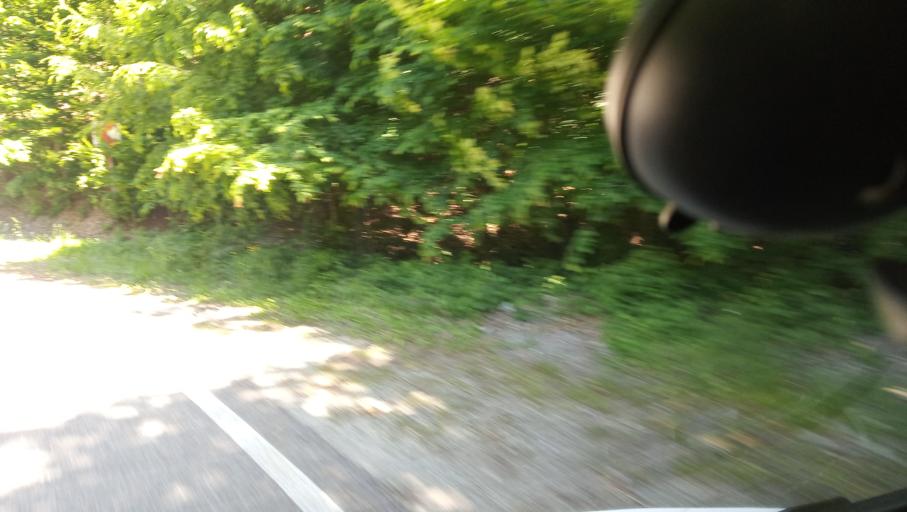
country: RO
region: Mehedinti
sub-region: Comuna Obarsia-Closani
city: Obarsia-Closani
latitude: 45.0491
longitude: 22.6251
